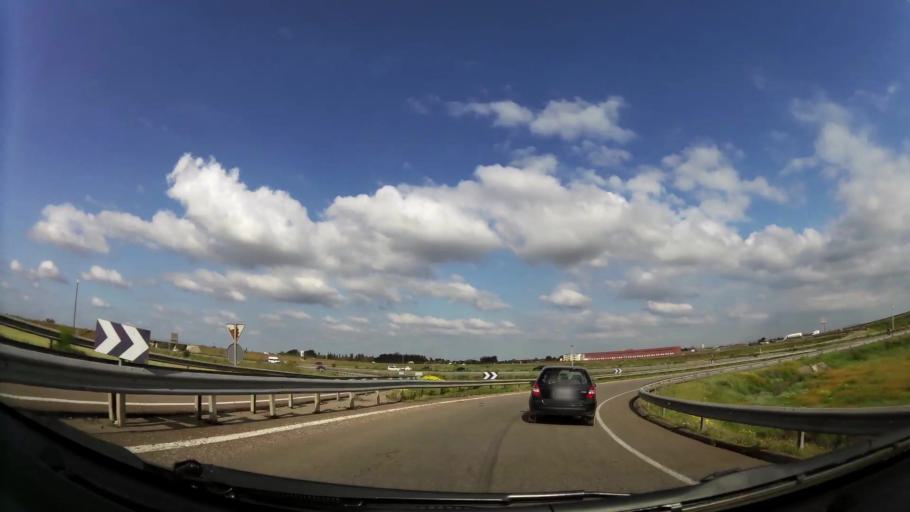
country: MA
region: Chaouia-Ouardigha
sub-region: Settat Province
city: Berrechid
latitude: 33.2467
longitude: -7.5651
